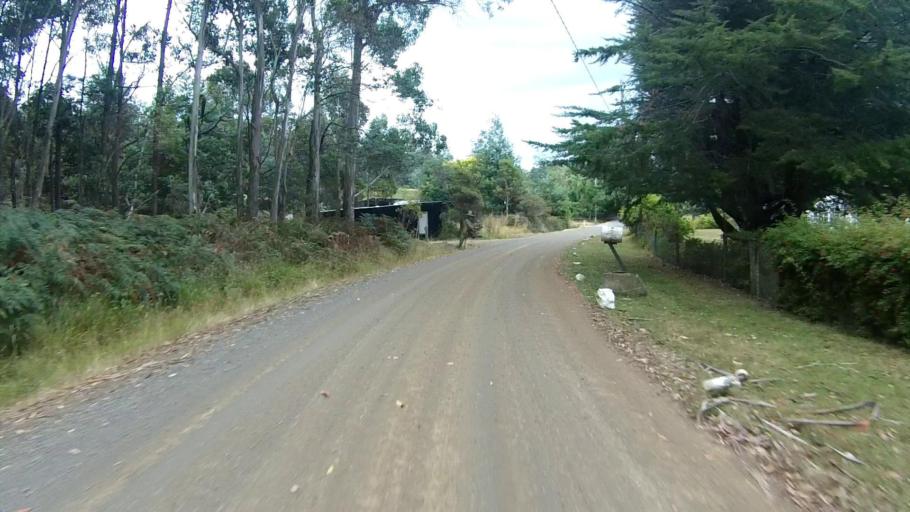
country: AU
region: Tasmania
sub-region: Huon Valley
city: Cygnet
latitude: -43.2324
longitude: 147.1589
